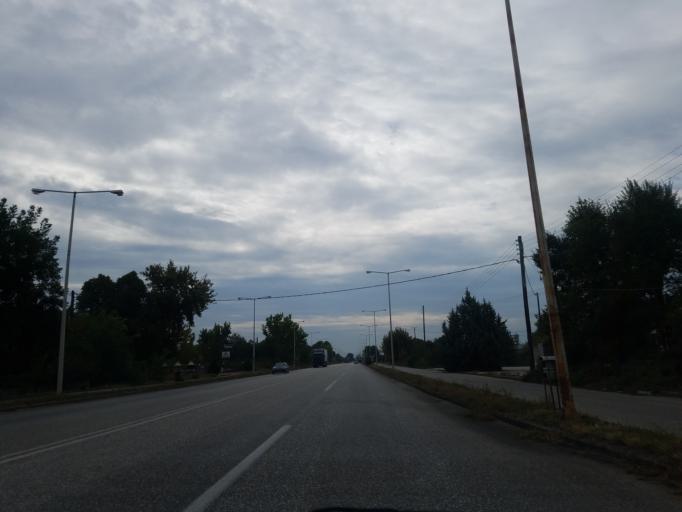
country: GR
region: Thessaly
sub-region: Trikala
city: Pyrgetos
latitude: 39.5803
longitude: 21.7420
